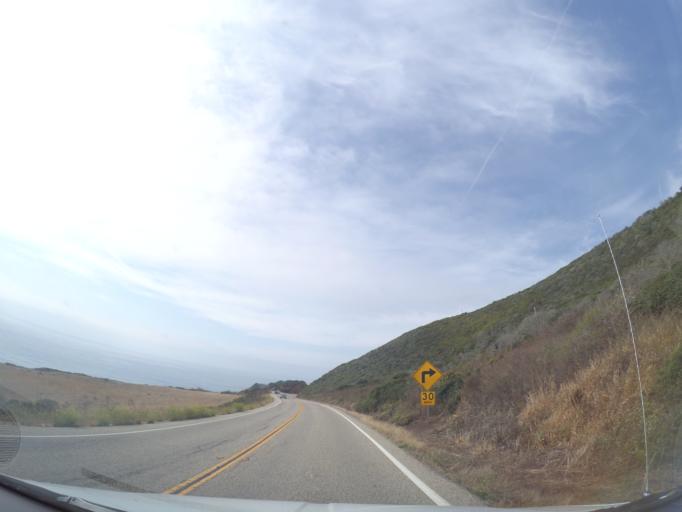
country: US
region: California
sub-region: Monterey County
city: Carmel-by-the-Sea
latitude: 36.3681
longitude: -121.9007
